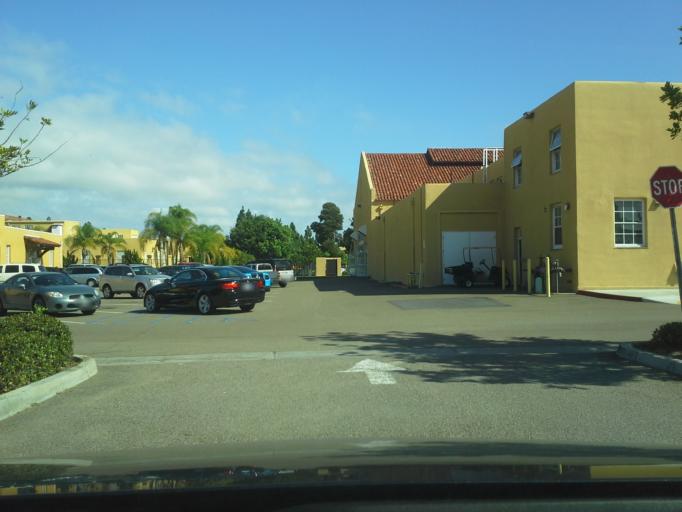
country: US
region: California
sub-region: San Diego County
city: San Diego
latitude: 32.7440
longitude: -117.1992
